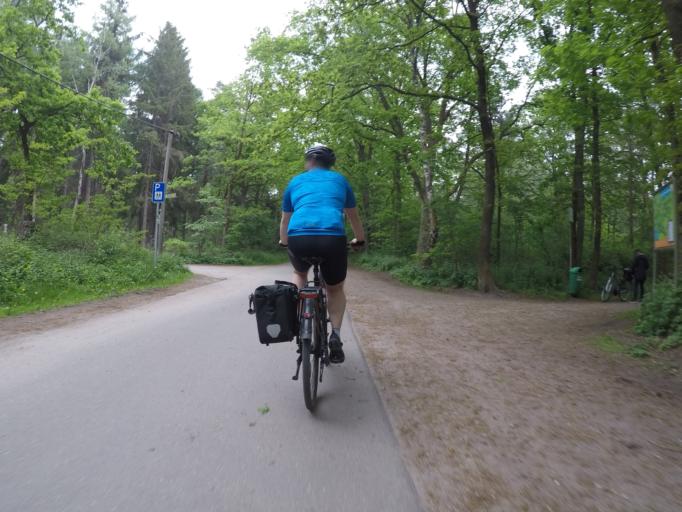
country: DE
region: Schleswig-Holstein
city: Norderstedt
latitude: 53.7111
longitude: 9.9735
